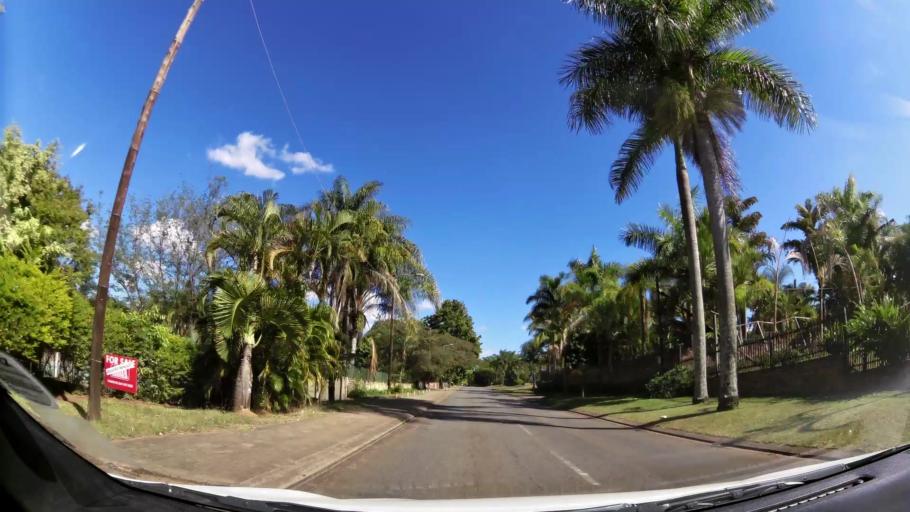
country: ZA
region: Limpopo
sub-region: Mopani District Municipality
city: Tzaneen
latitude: -23.8175
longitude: 30.1546
